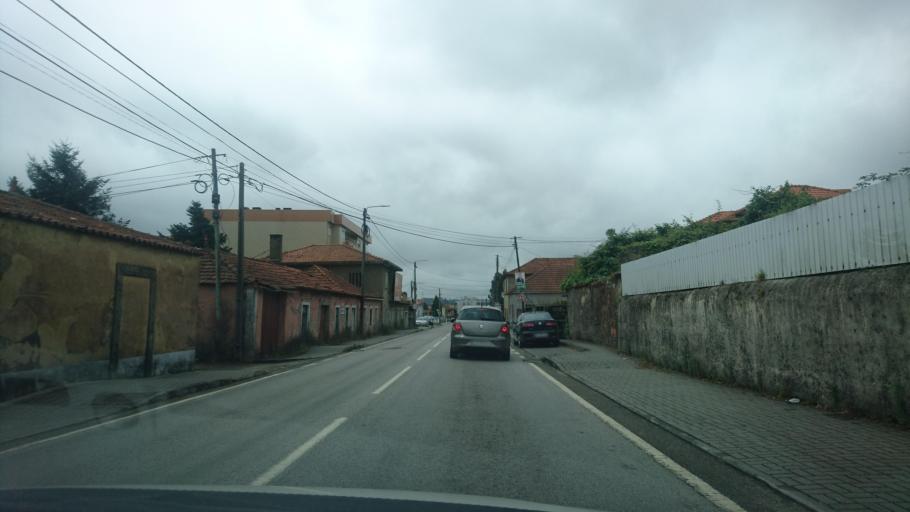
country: PT
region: Aveiro
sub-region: Santa Maria da Feira
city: Fiaes
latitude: 40.9913
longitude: -8.5385
